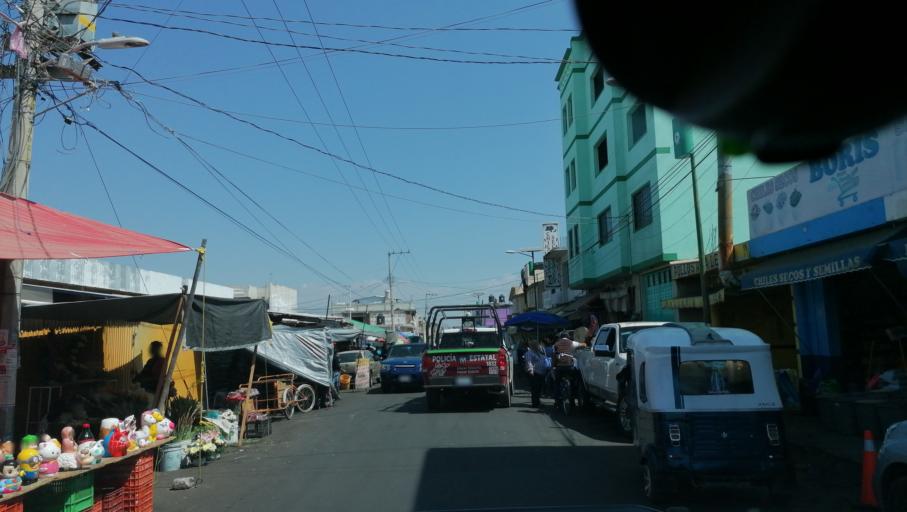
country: MX
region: Puebla
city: Huejotzingo
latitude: 19.1572
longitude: -98.4126
